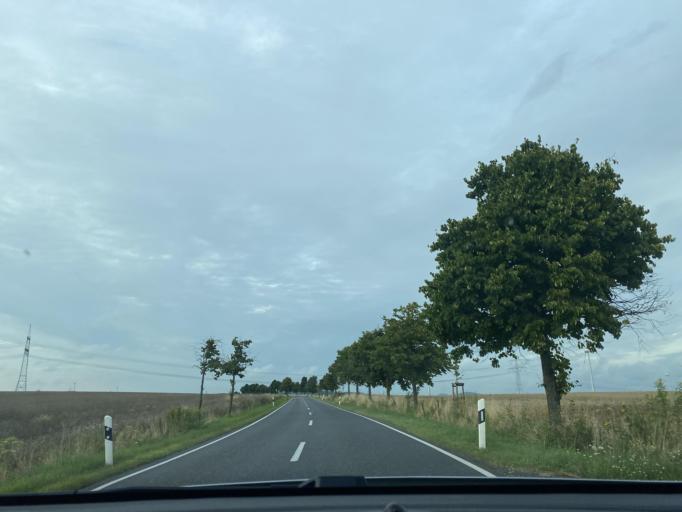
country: DE
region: Saxony
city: Bernstadt
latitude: 51.0275
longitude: 14.8095
